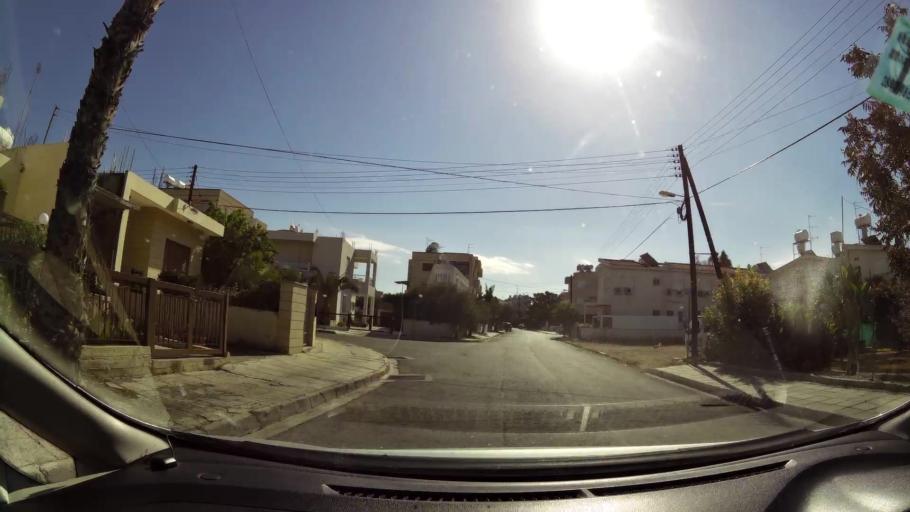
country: CY
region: Lefkosia
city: Nicosia
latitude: 35.1376
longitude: 33.3453
